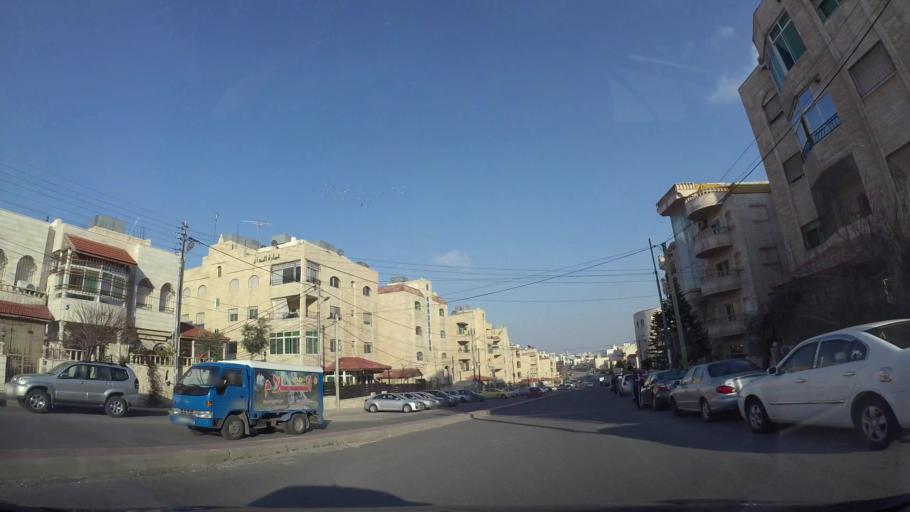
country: JO
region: Amman
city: Amman
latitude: 31.9861
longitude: 35.9433
